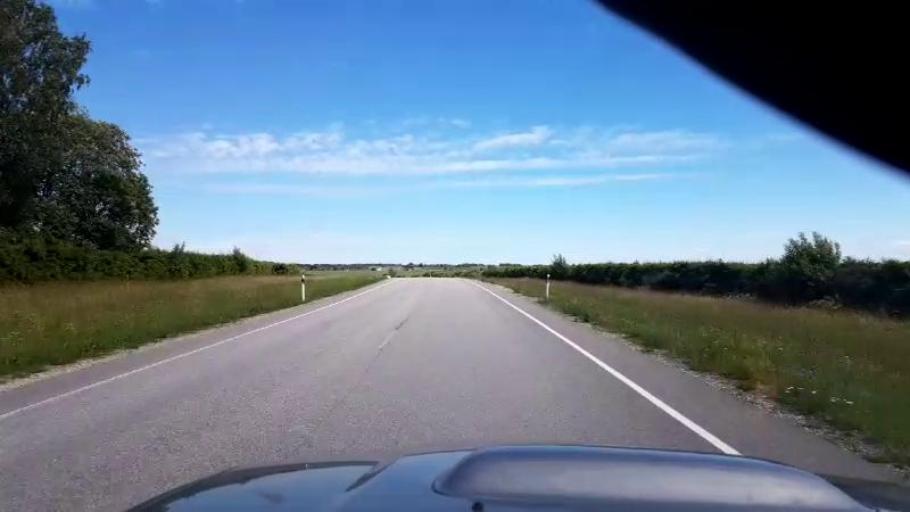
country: EE
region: Jaervamaa
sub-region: Koeru vald
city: Koeru
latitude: 58.9779
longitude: 26.0658
